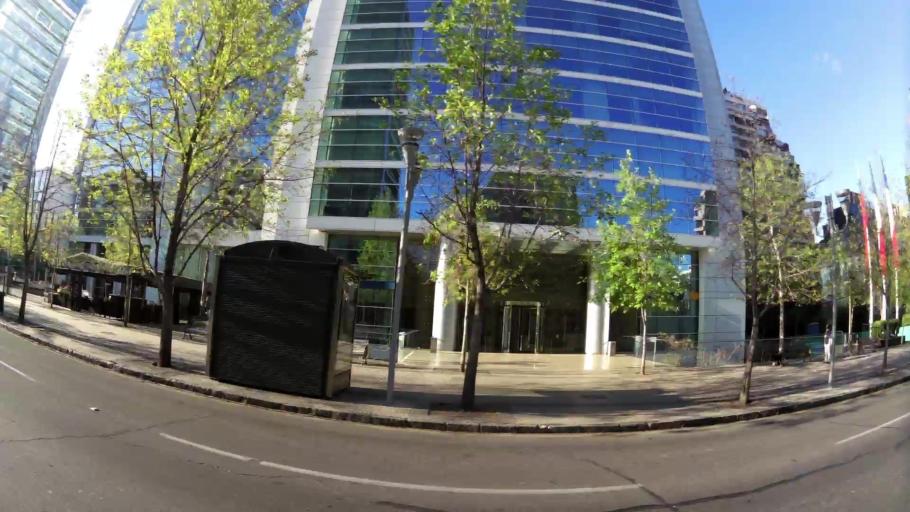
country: CL
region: Santiago Metropolitan
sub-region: Provincia de Santiago
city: Villa Presidente Frei, Nunoa, Santiago, Chile
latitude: -33.4146
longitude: -70.5943
